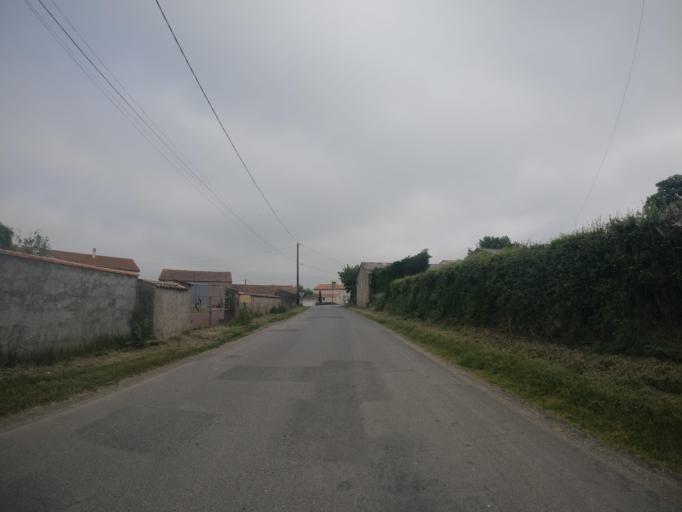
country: FR
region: Poitou-Charentes
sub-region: Departement des Deux-Sevres
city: Chiche
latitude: 46.8243
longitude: -0.3788
